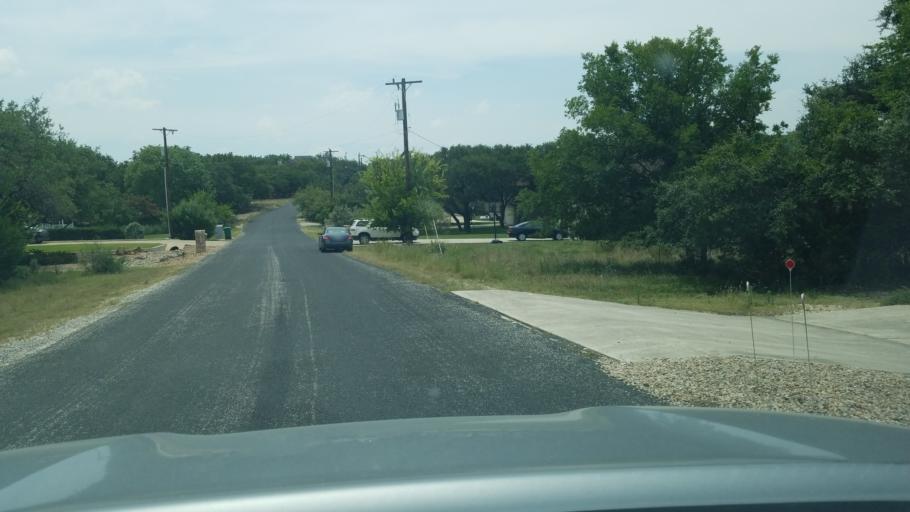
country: US
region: Texas
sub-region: Bexar County
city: Timberwood Park
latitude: 29.6930
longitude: -98.5016
